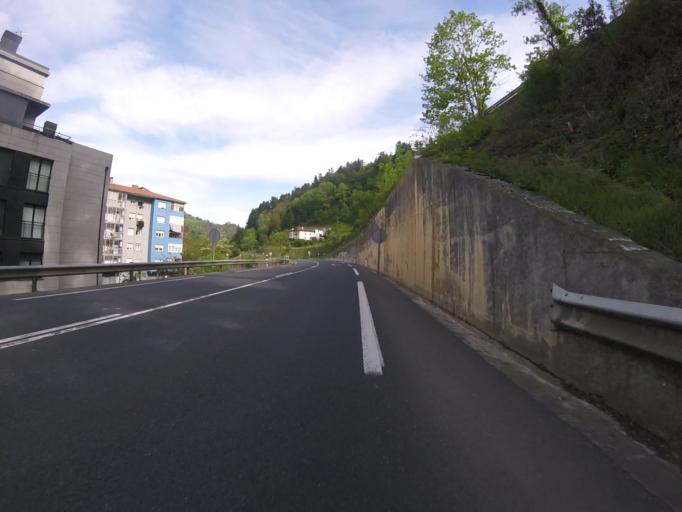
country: ES
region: Basque Country
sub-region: Provincia de Guipuzcoa
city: Zumarraga
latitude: 43.0943
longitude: -2.3117
